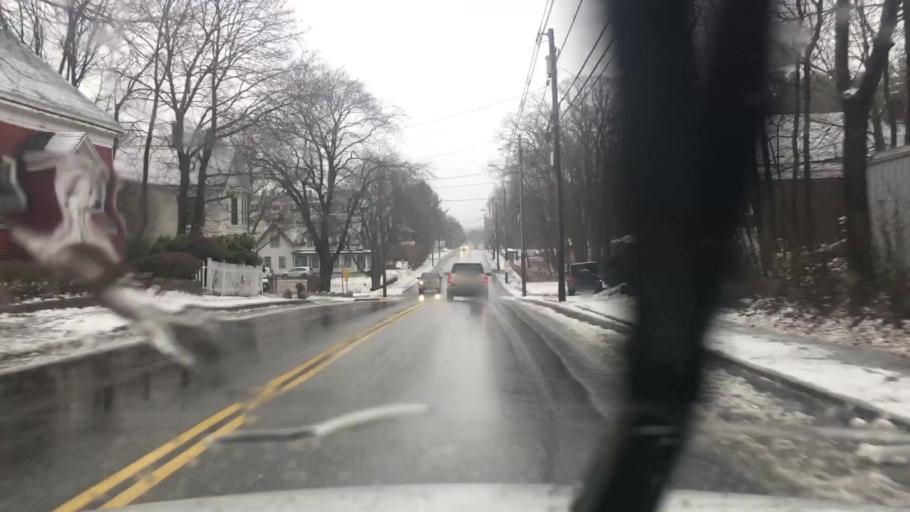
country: US
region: Maine
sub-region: York County
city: Biddeford
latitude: 43.4885
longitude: -70.4504
